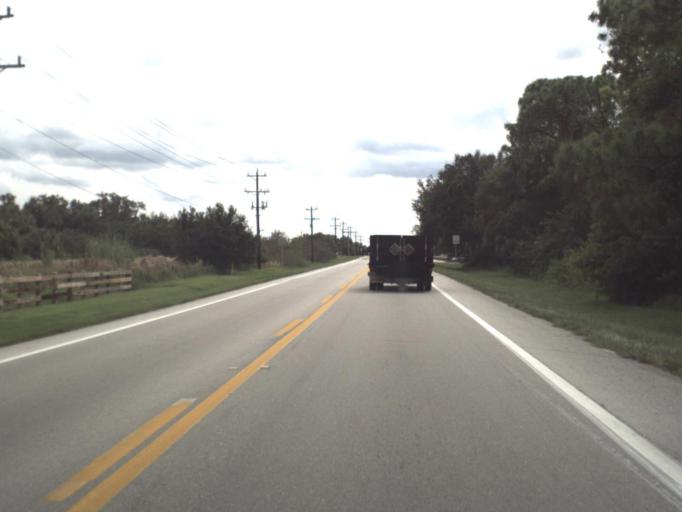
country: US
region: Florida
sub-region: Lee County
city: Fort Myers Shores
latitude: 26.7285
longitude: -81.7610
